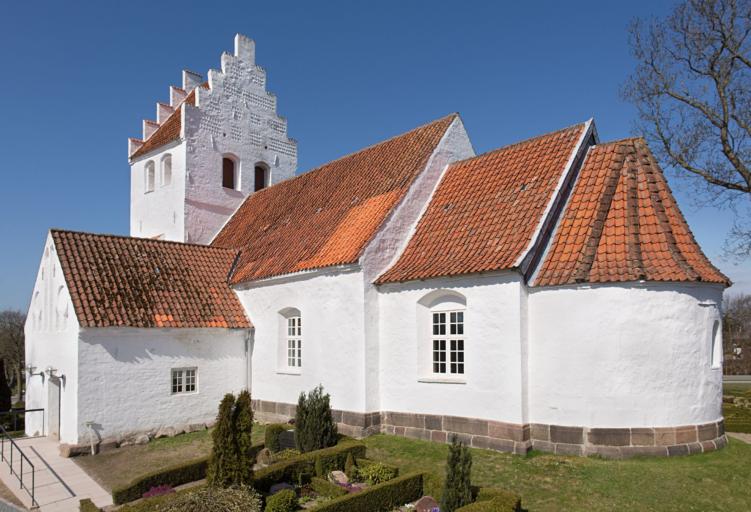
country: DK
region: South Denmark
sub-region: Odense Kommune
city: Bellinge
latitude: 55.3408
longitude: 10.3608
